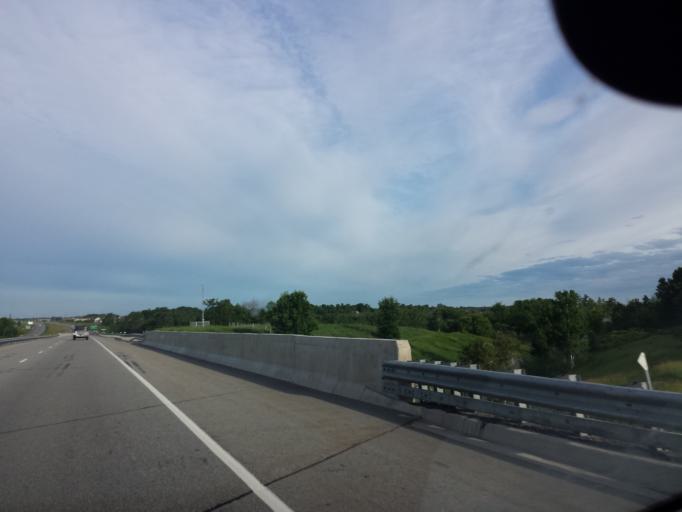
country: CA
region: Ontario
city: Arnprior
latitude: 45.4201
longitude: -76.3436
